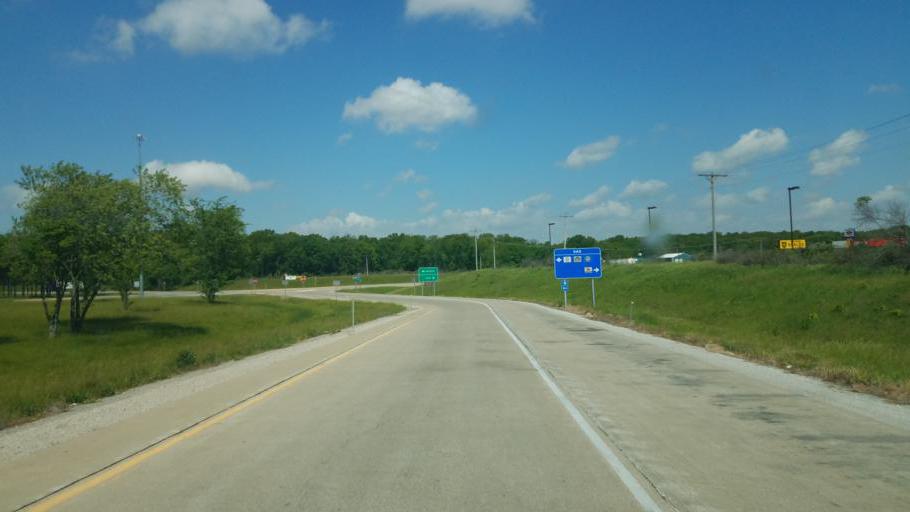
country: US
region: Illinois
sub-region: Clark County
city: Marshall
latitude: 39.4228
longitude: -87.6910
